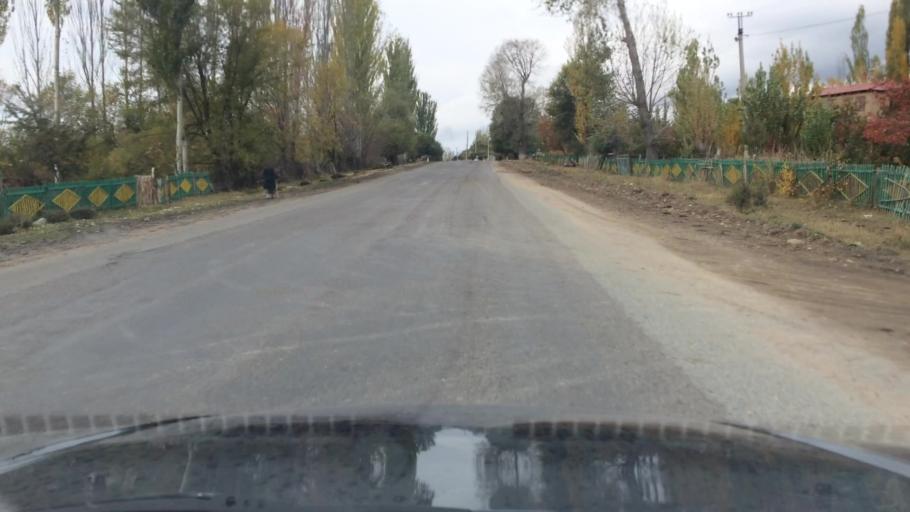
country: KG
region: Ysyk-Koel
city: Pokrovka
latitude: 42.7370
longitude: 77.9470
